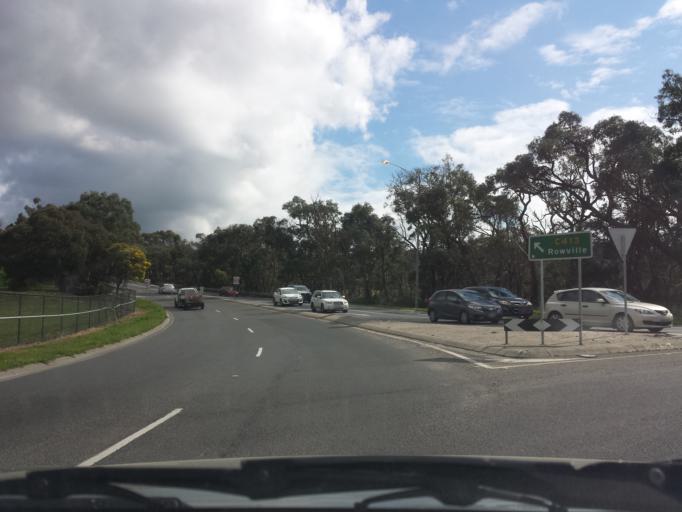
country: AU
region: Victoria
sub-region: Yarra Ranges
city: Belgrave South
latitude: -37.9540
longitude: 145.3474
